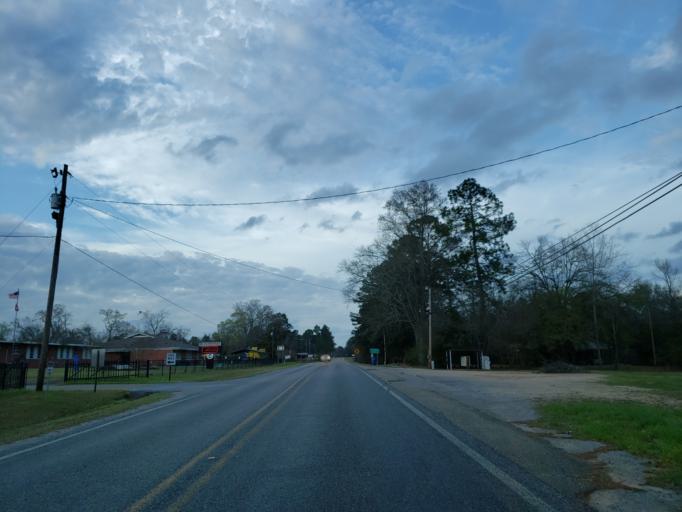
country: US
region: Mississippi
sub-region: Clarke County
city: Stonewall
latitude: 32.2249
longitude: -88.7002
